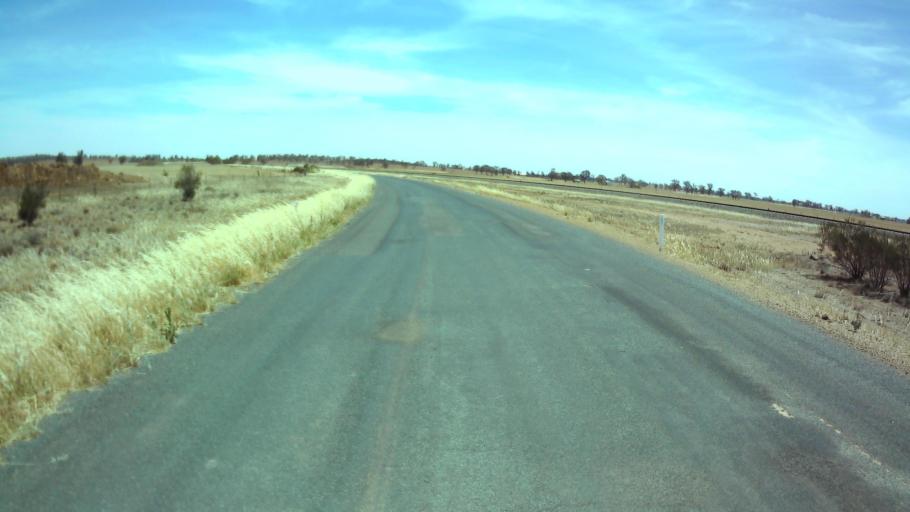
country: AU
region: New South Wales
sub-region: Weddin
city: Grenfell
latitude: -33.7543
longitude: 147.7642
